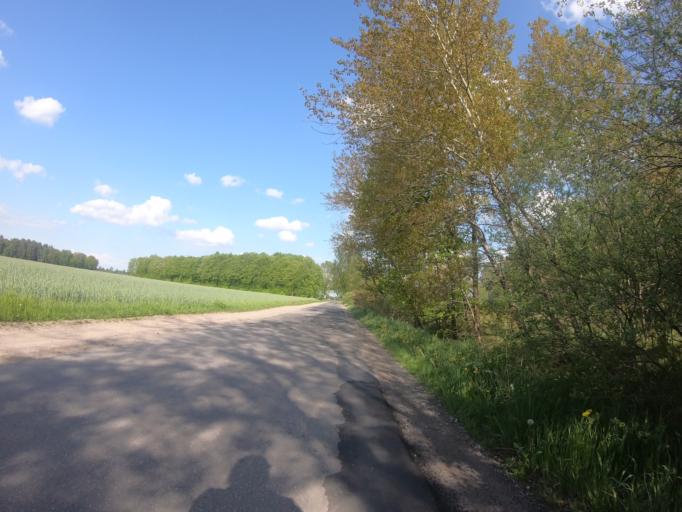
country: DE
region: Lower Saxony
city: Gifhorn
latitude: 52.5276
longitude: 10.5776
